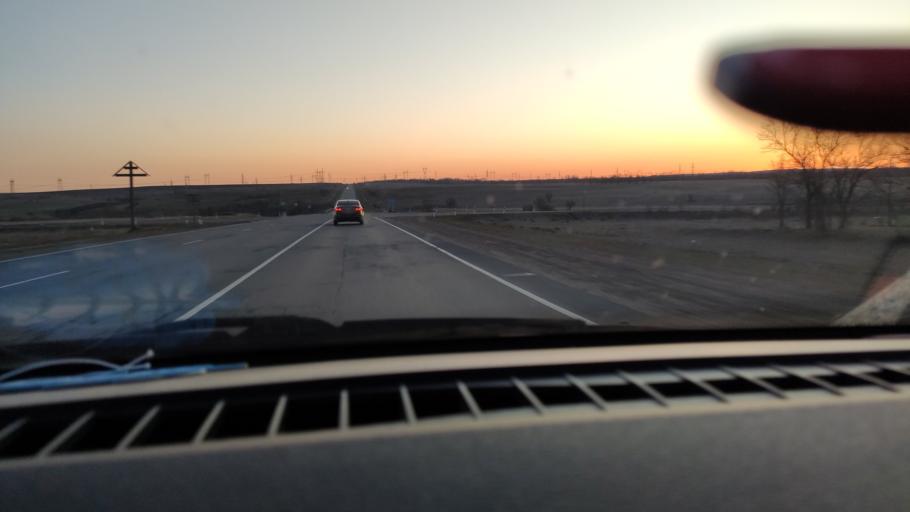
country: RU
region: Saratov
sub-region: Saratovskiy Rayon
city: Saratov
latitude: 51.7530
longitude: 46.0628
